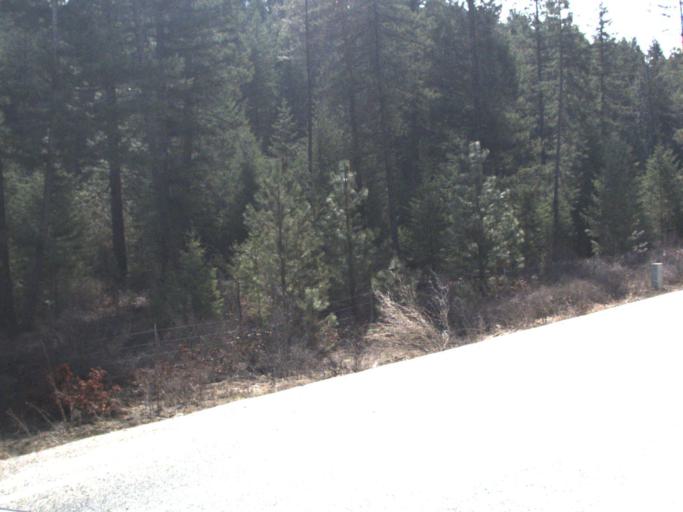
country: US
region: Washington
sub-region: Stevens County
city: Colville
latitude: 48.5325
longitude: -117.8220
